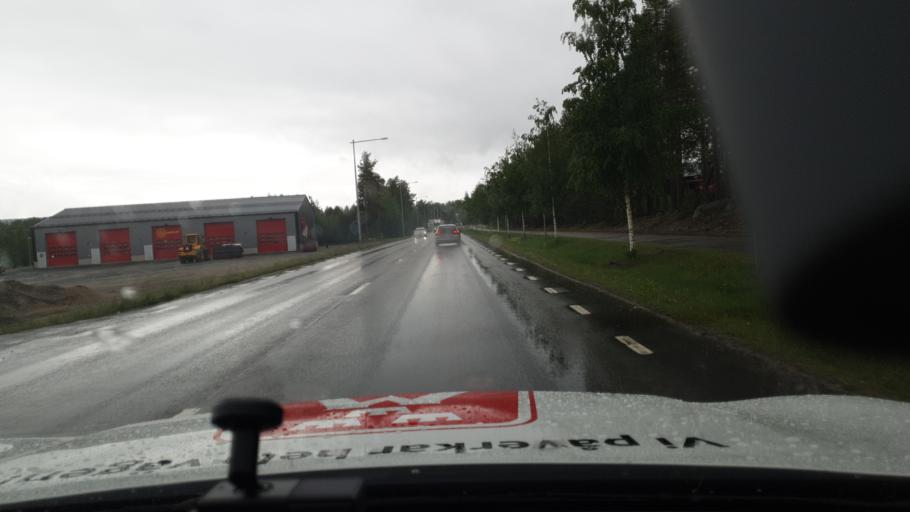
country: SE
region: Vaesterbotten
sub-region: Lycksele Kommun
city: Lycksele
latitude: 64.5822
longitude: 18.6999
